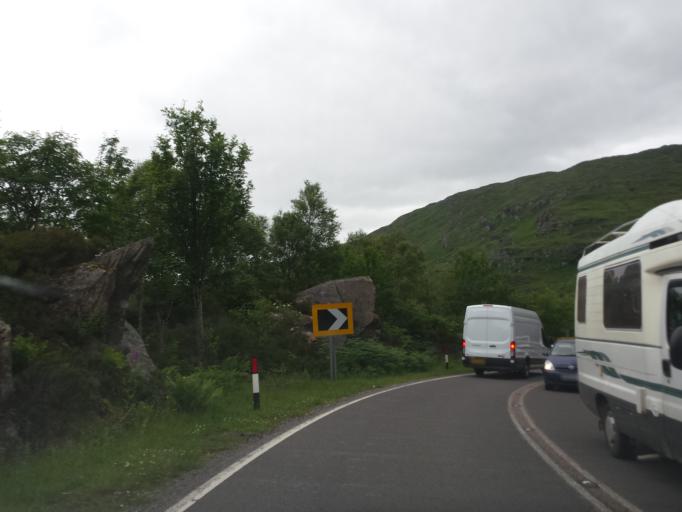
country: GB
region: Scotland
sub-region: Argyll and Bute
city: Isle Of Mull
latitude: 56.8833
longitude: -5.6306
